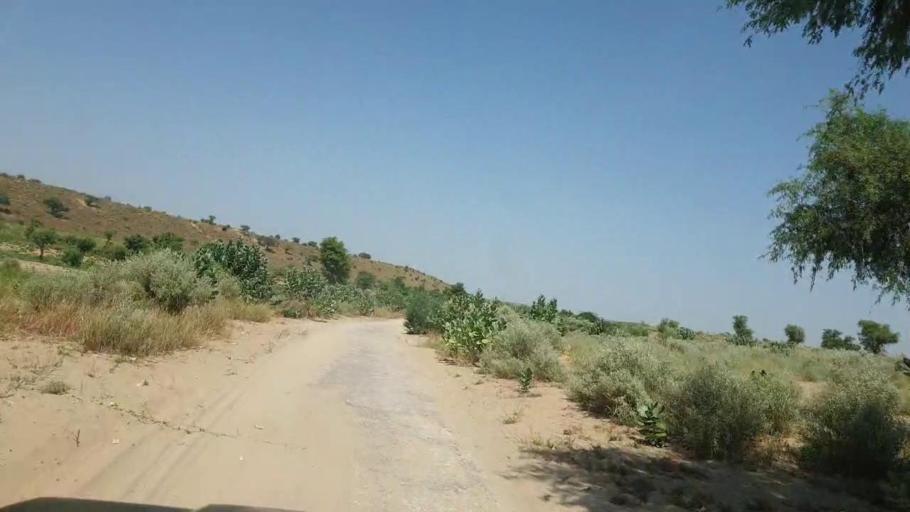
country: PK
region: Sindh
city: Chor
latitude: 25.3857
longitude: 70.3123
